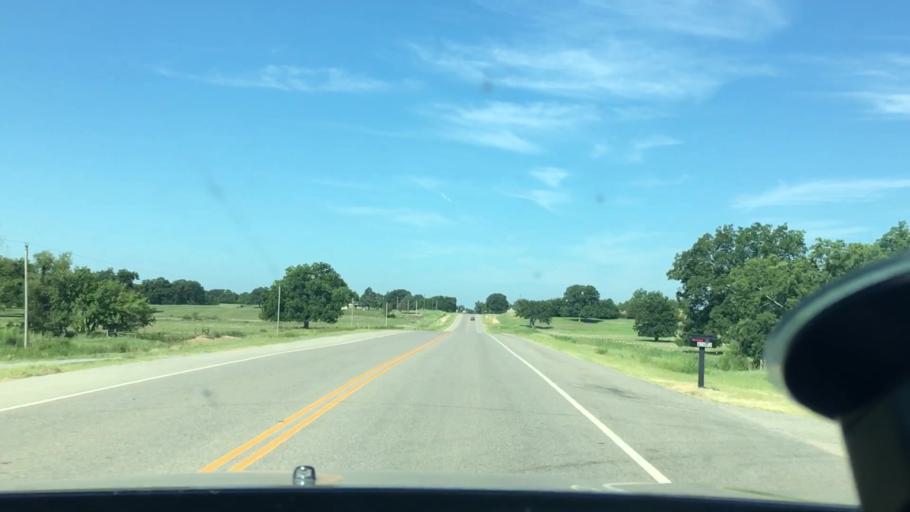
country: US
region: Oklahoma
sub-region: Johnston County
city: Tishomingo
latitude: 34.2742
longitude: -96.5420
